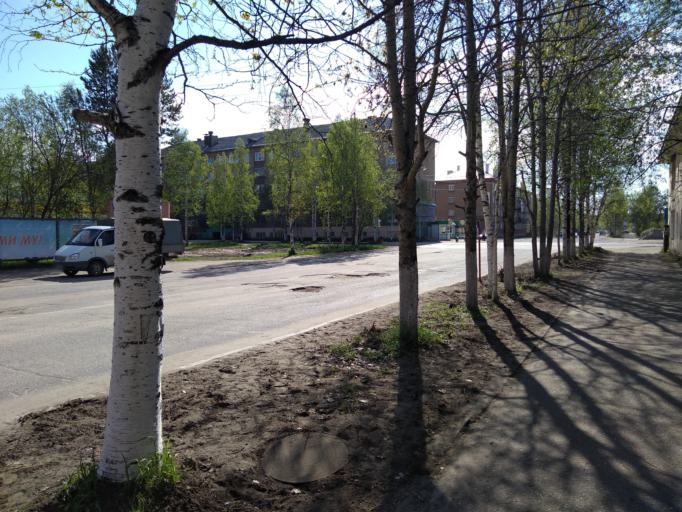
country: RU
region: Komi Republic
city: Pechora
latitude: 65.1143
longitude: 57.1600
